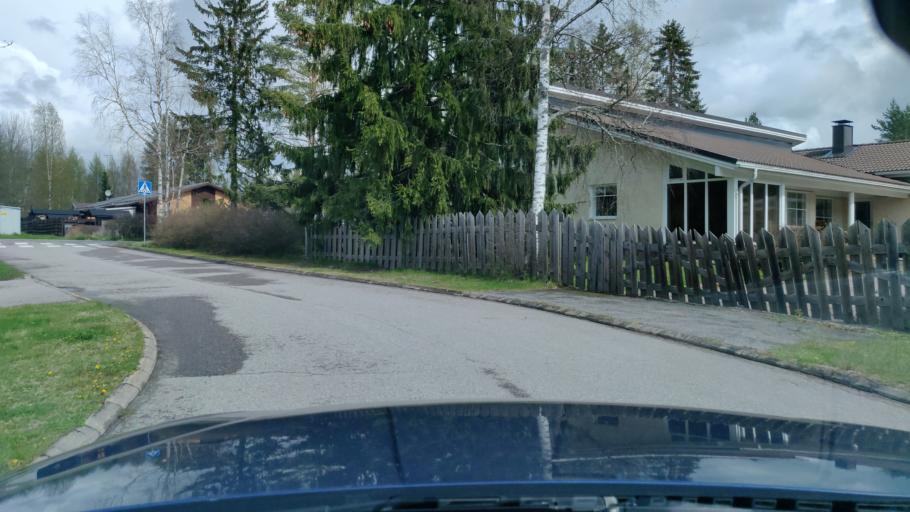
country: FI
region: Uusimaa
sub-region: Helsinki
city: Nurmijaervi
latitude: 60.3621
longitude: 24.7386
